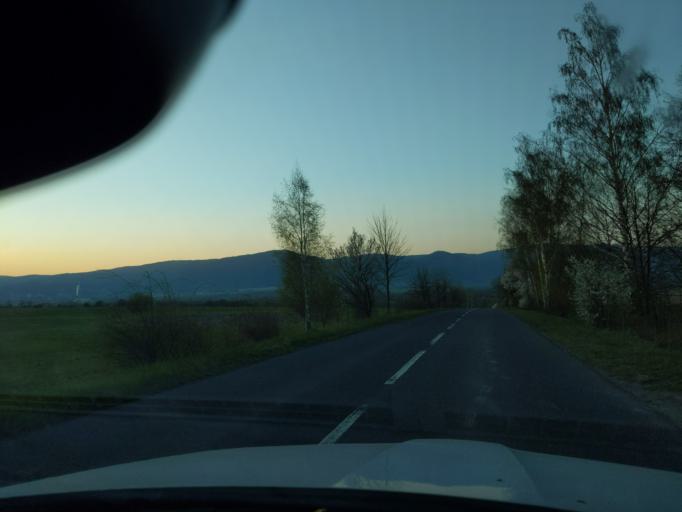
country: CZ
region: Ustecky
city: Chabarovice
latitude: 50.6553
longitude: 13.9149
